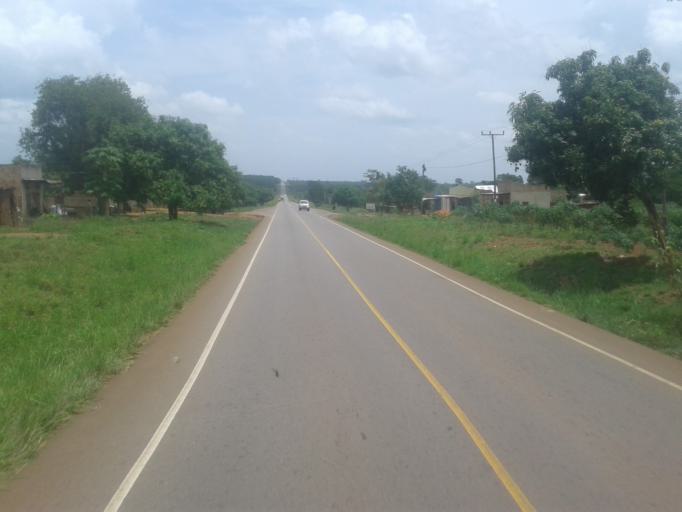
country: UG
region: Central Region
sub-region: Nakasongola District
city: Nakasongola
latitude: 1.3990
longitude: 32.3118
